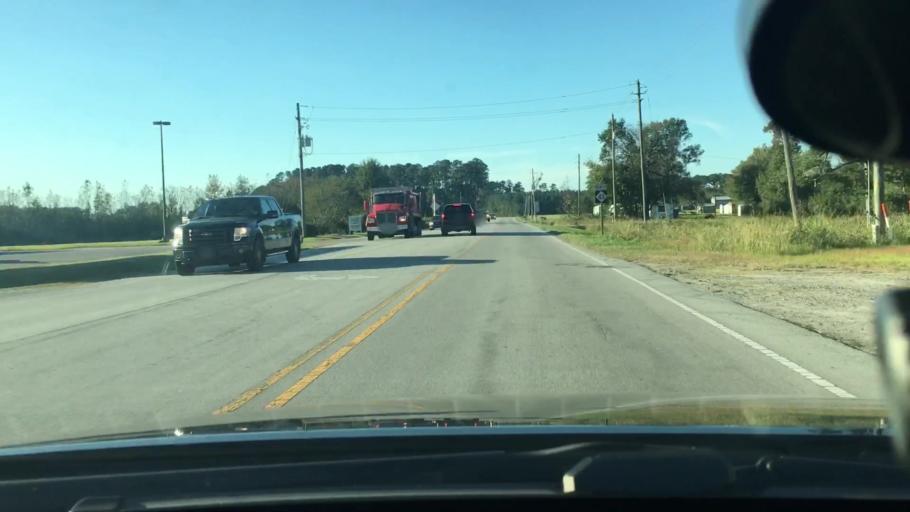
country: US
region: North Carolina
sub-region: Pitt County
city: Windsor
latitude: 35.4645
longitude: -77.2751
